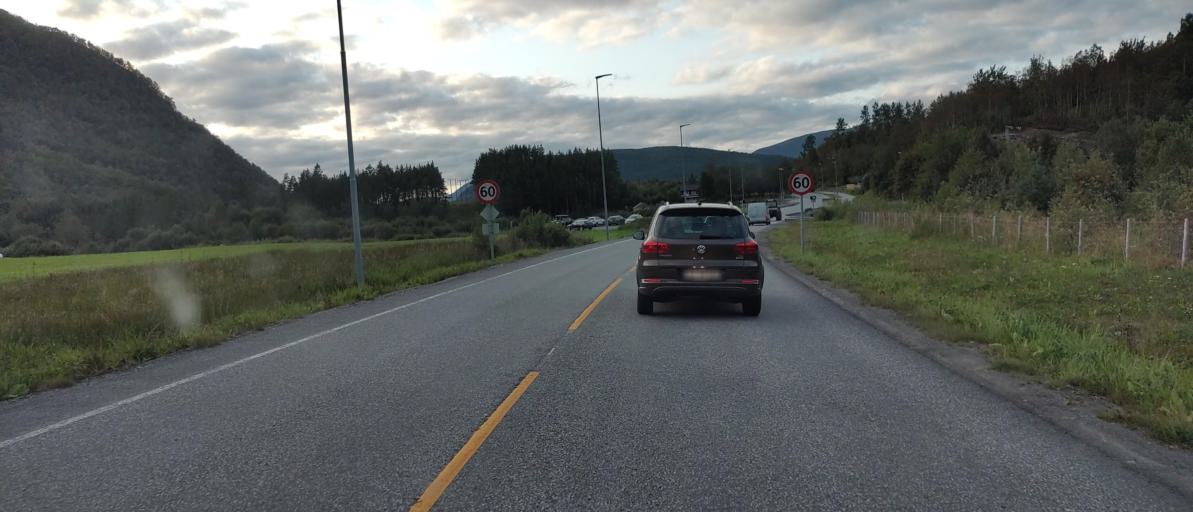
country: NO
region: More og Romsdal
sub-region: Molde
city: Molde
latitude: 62.7907
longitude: 7.2330
